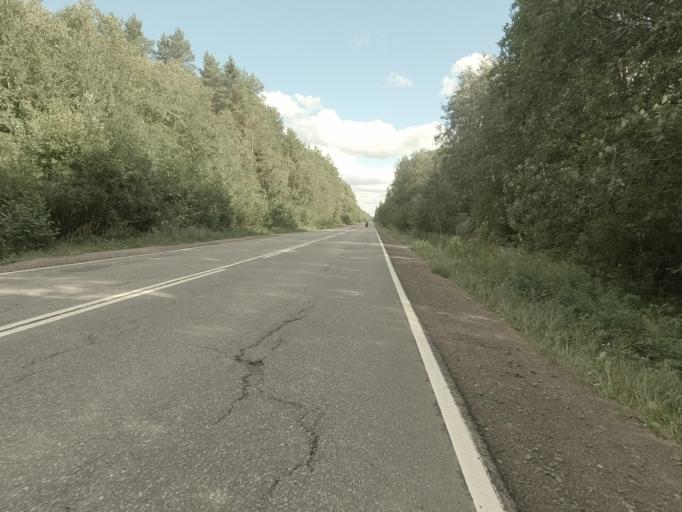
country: RU
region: Leningrad
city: Shcheglovo
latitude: 60.0067
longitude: 30.8626
